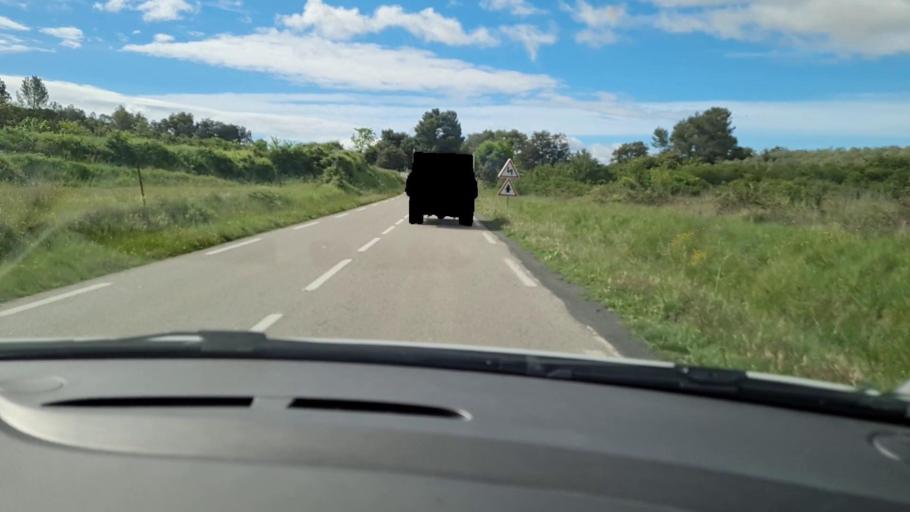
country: FR
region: Languedoc-Roussillon
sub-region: Departement du Gard
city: Sommieres
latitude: 43.8200
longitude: 4.0512
